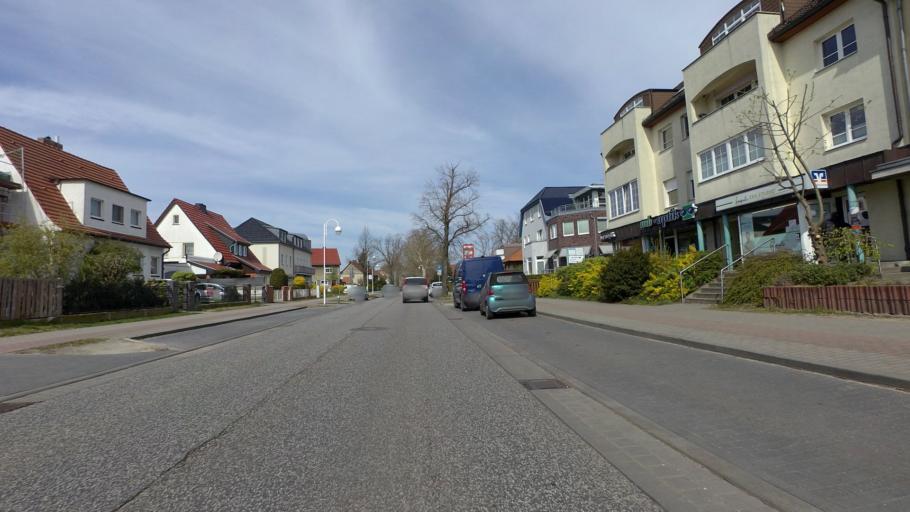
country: DE
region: Berlin
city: Lichtenrade
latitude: 52.3611
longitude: 13.4111
